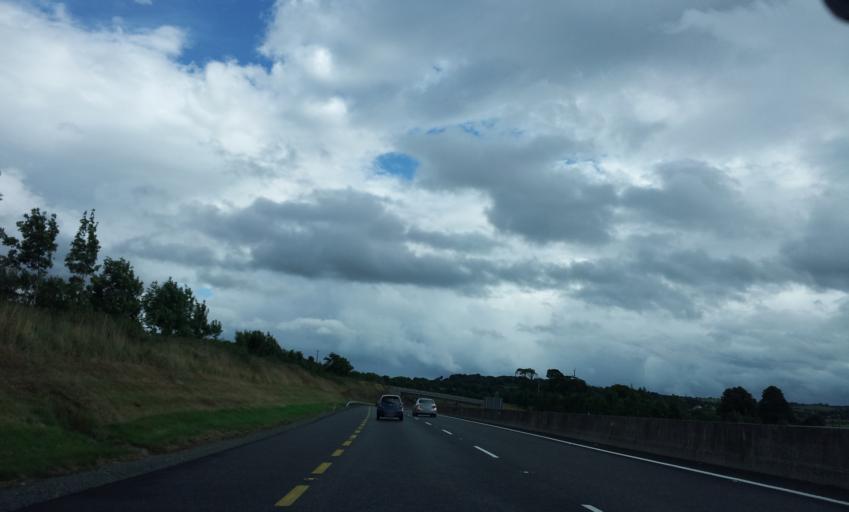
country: IE
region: Leinster
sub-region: Kilkenny
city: Mooncoin
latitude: 52.2470
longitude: -7.1905
